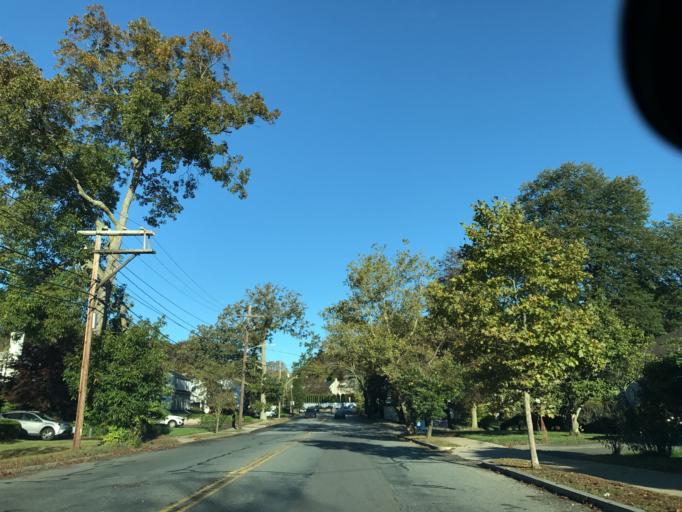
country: US
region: Massachusetts
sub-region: Middlesex County
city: Newton
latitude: 42.2967
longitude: -71.1818
